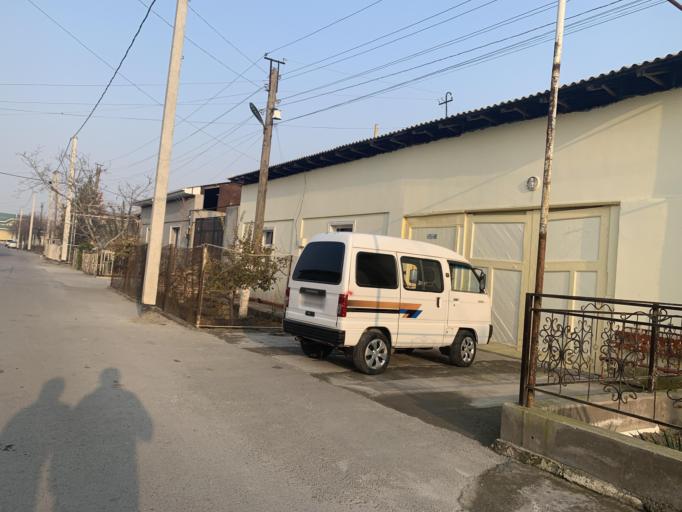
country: UZ
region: Fergana
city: Qo`qon
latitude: 40.5409
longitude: 70.9258
